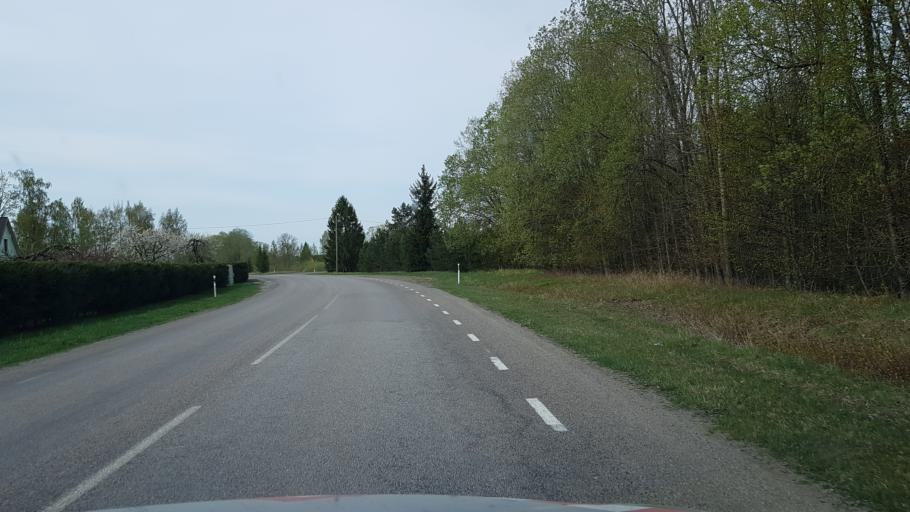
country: EE
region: Paernumaa
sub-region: Audru vald
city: Audru
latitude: 58.3666
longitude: 24.2649
